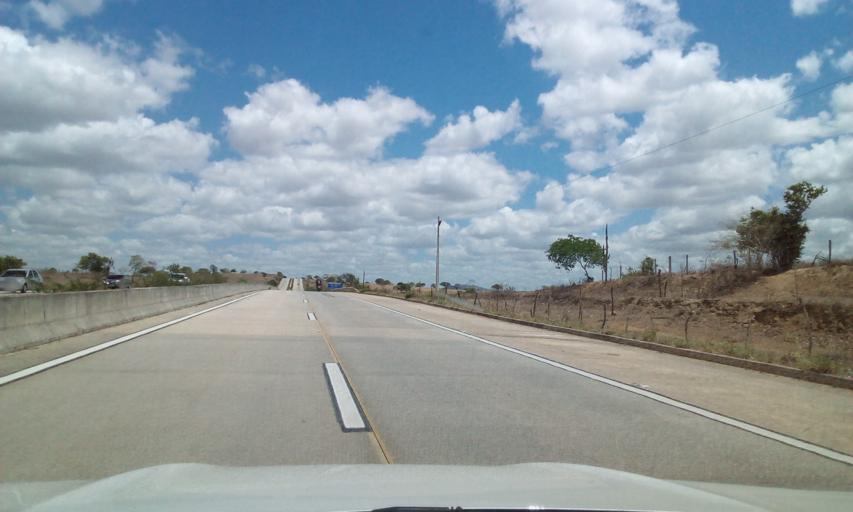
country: BR
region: Alagoas
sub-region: Porto Real Do Colegio
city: Porto Real do Colegio
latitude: -10.1458
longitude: -36.8060
